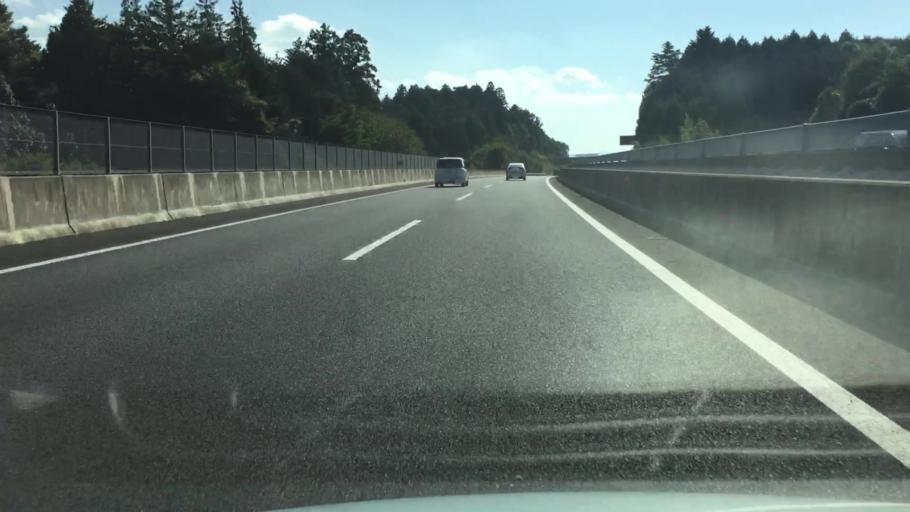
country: JP
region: Ibaraki
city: Tomobe
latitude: 36.3379
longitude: 140.2805
